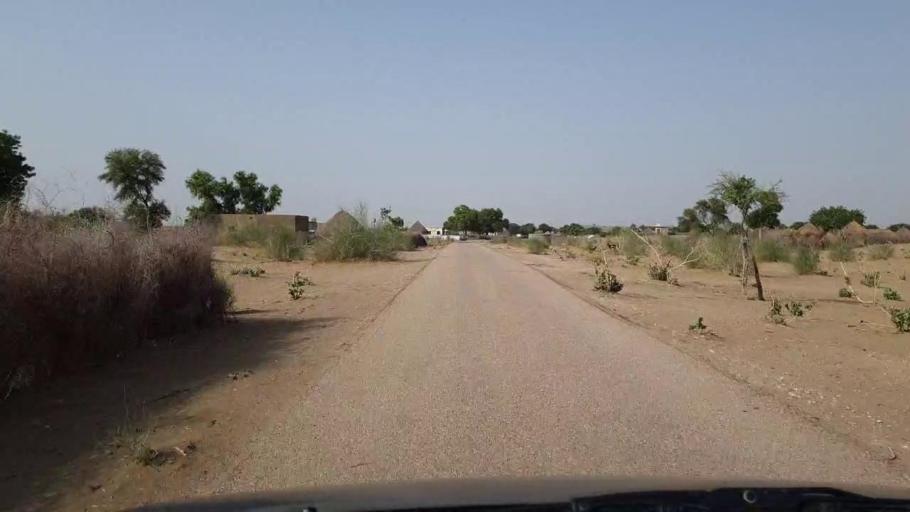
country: PK
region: Sindh
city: Chor
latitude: 25.4540
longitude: 70.5316
